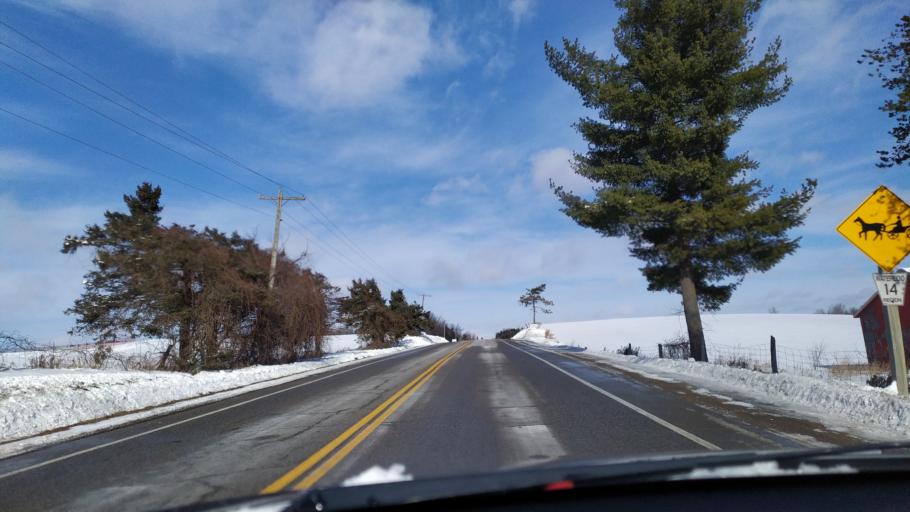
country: CA
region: Ontario
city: Waterloo
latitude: 43.4757
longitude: -80.6908
